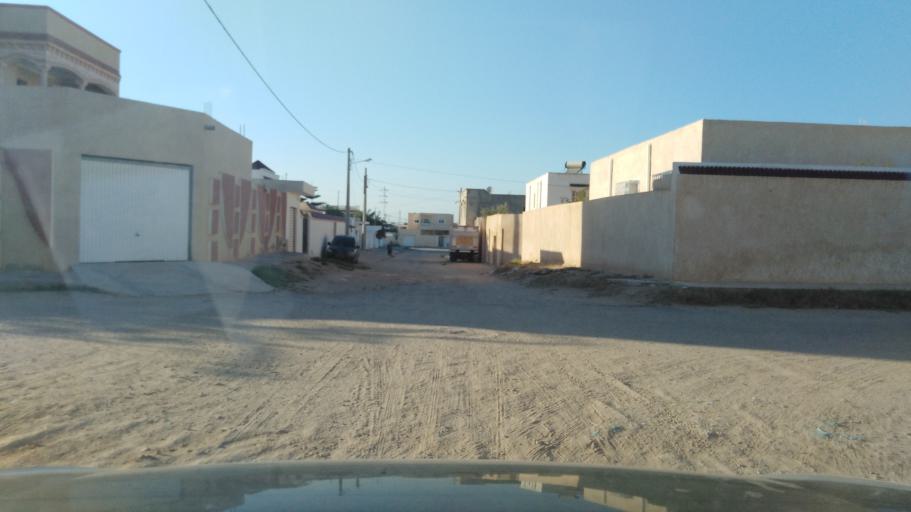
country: TN
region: Qabis
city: Gabes
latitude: 33.9520
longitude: 10.0122
